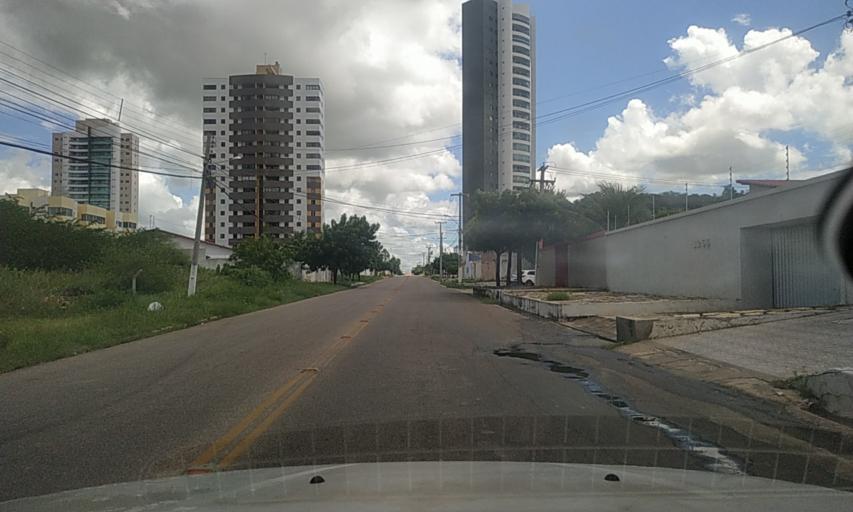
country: BR
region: Rio Grande do Norte
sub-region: Mossoro
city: Mossoro
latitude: -5.1797
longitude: -37.3609
